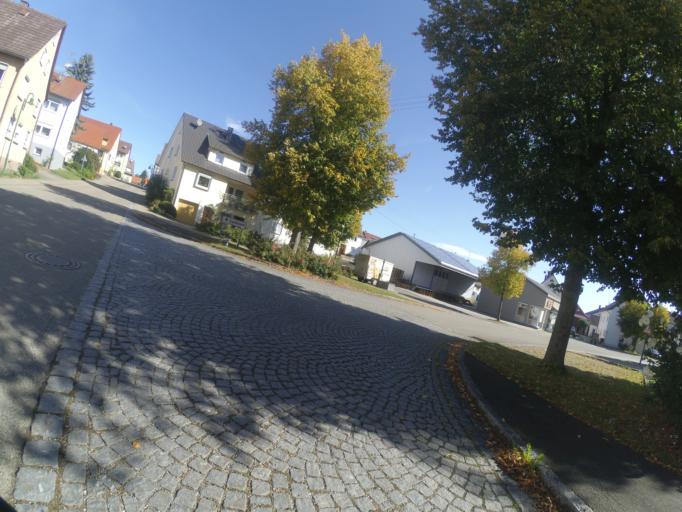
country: DE
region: Baden-Wuerttemberg
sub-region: Tuebingen Region
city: Ballendorf
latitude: 48.5544
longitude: 10.0772
